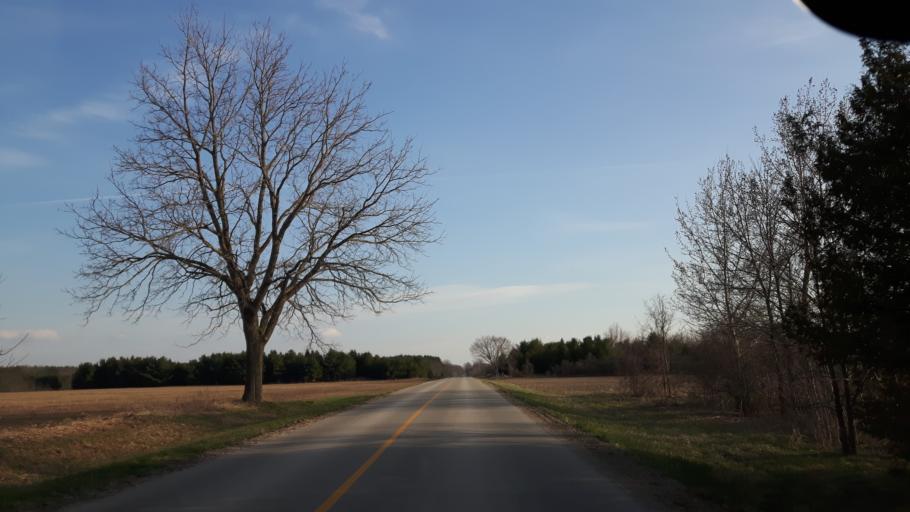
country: CA
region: Ontario
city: Goderich
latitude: 43.6668
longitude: -81.6643
